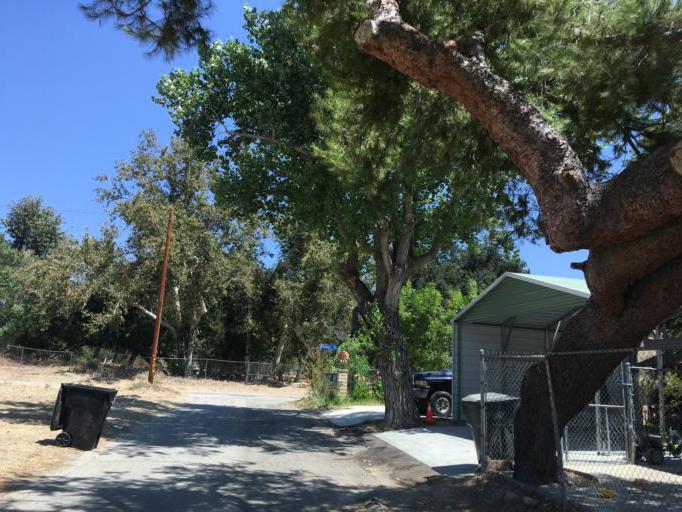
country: US
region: California
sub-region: Los Angeles County
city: Val Verde
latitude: 34.4419
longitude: -118.6565
